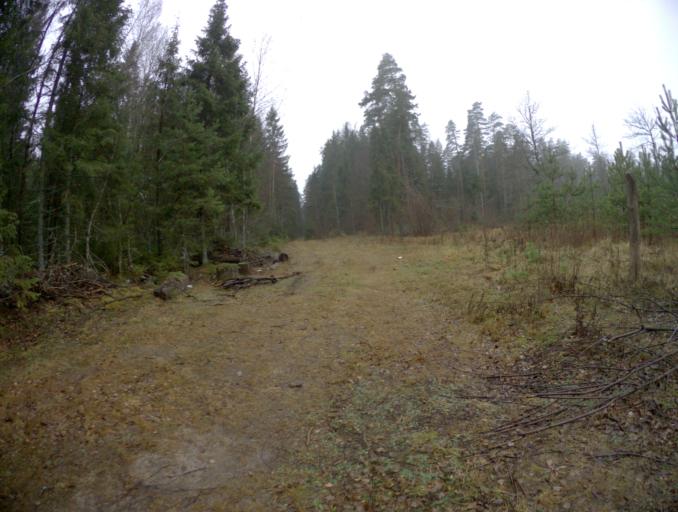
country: RU
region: Vladimir
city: Golovino
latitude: 56.0086
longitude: 40.4830
